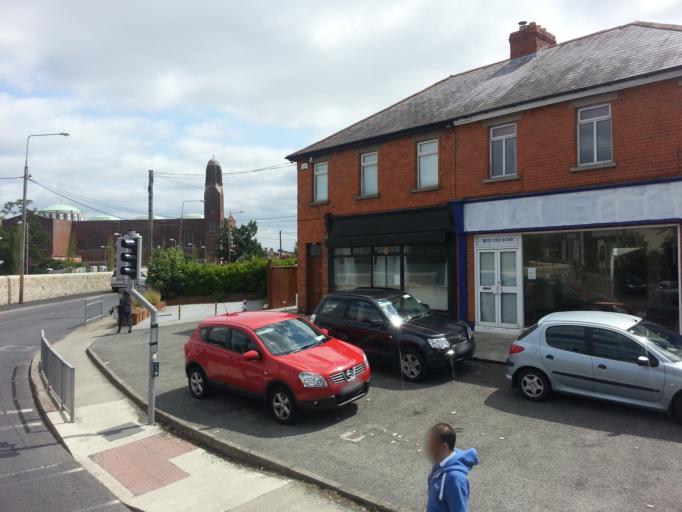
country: IE
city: Milltown
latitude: 53.3051
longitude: -6.2457
